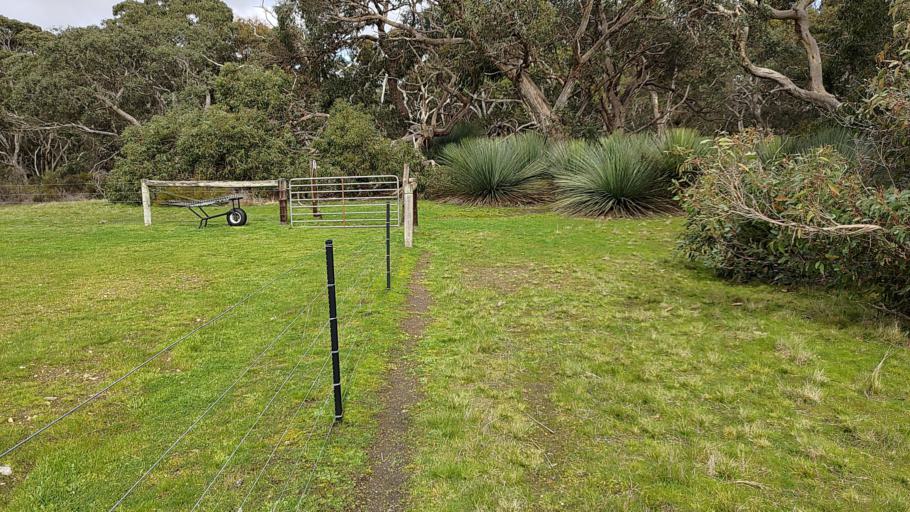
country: AU
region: South Australia
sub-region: Kangaroo Island
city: Kingscote
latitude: -35.7334
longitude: 137.2205
